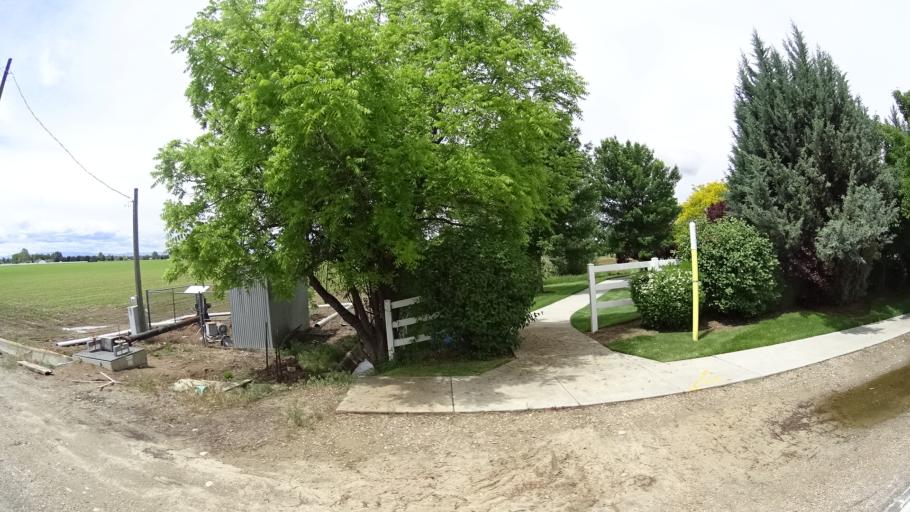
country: US
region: Idaho
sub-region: Ada County
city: Eagle
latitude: 43.7099
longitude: -116.4035
